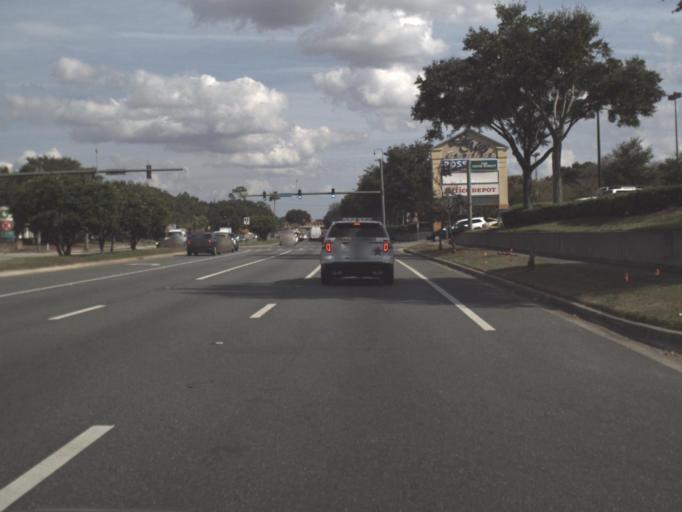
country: US
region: Florida
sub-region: Seminole County
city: Heathrow
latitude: 28.7561
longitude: -81.3559
